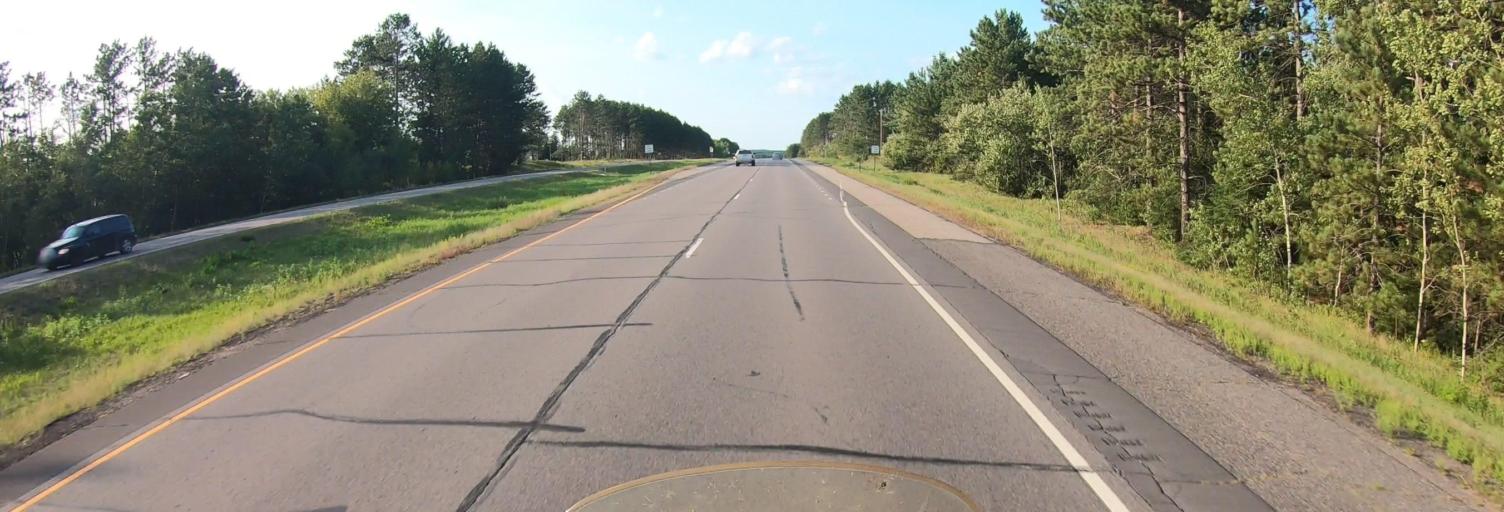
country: US
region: Minnesota
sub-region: Saint Louis County
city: Eveleth
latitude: 47.4148
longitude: -92.5211
